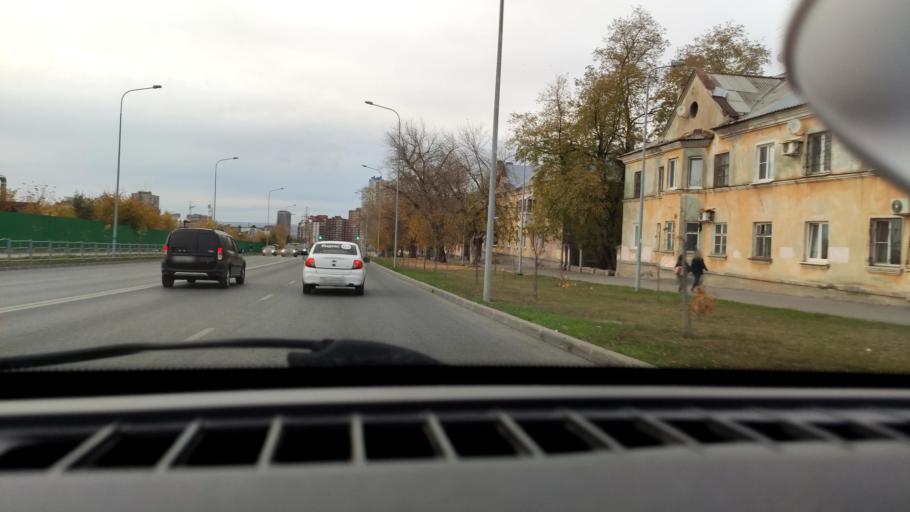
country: RU
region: Samara
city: Samara
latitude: 53.2075
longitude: 50.1545
